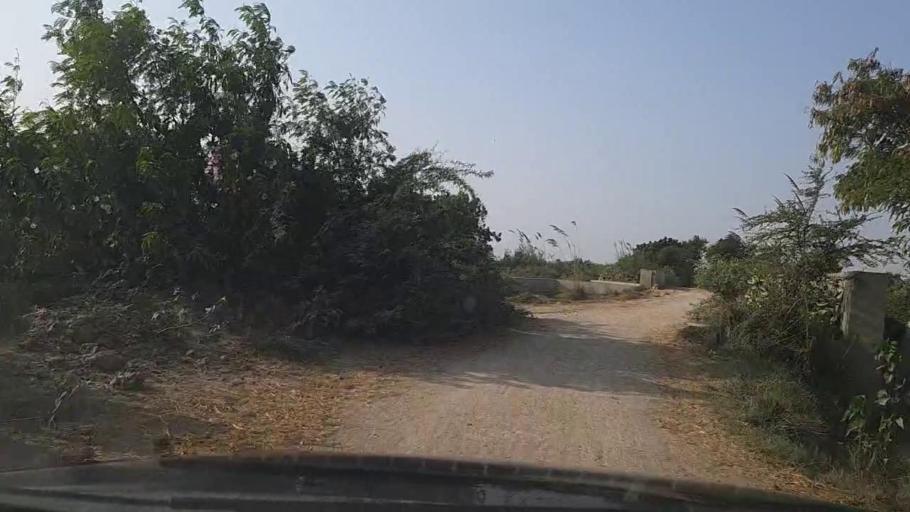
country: PK
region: Sindh
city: Mirpur Sakro
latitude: 24.6393
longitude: 67.7455
